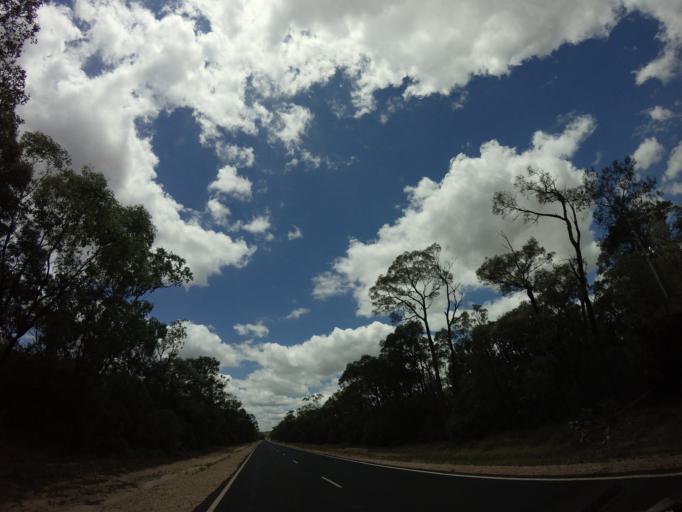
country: AU
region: Queensland
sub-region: Goondiwindi
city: Goondiwindi
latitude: -28.0432
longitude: 150.7941
